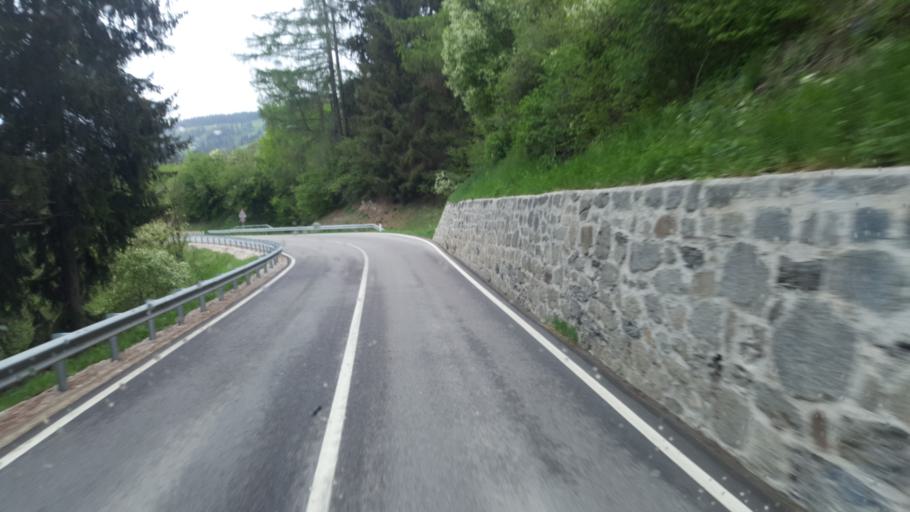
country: IT
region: Trentino-Alto Adige
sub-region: Bolzano
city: Monguelfo
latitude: 46.7604
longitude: 12.0962
